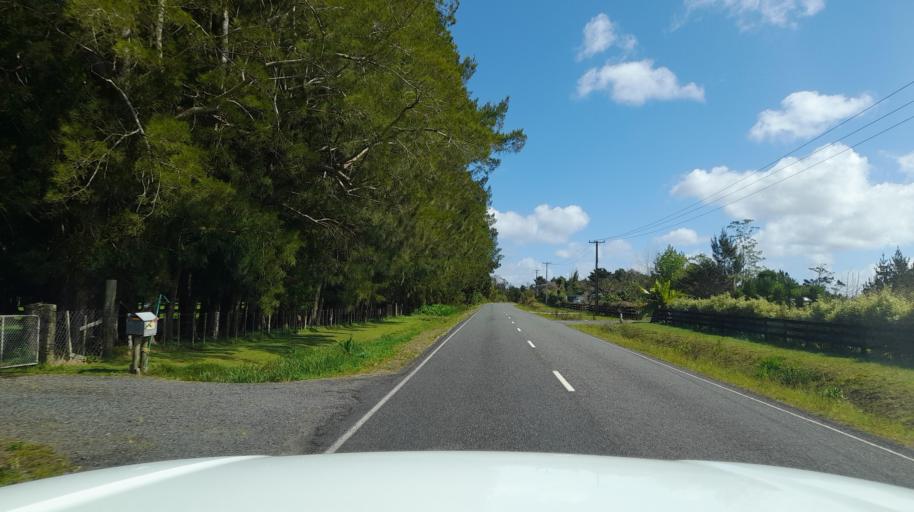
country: NZ
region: Northland
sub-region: Far North District
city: Kerikeri
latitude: -35.2411
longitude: 173.8894
